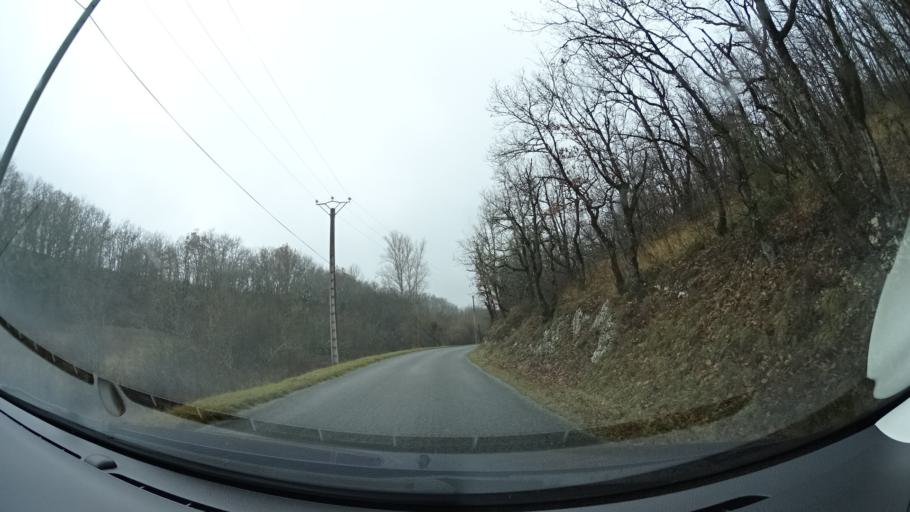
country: FR
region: Midi-Pyrenees
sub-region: Departement du Lot
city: Montcuq
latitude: 44.3882
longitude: 1.2235
